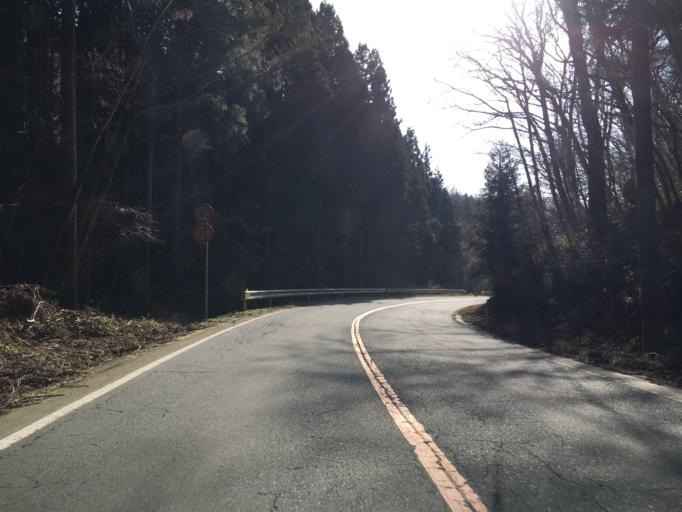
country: JP
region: Ibaraki
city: Hitachi
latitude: 36.7374
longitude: 140.5330
